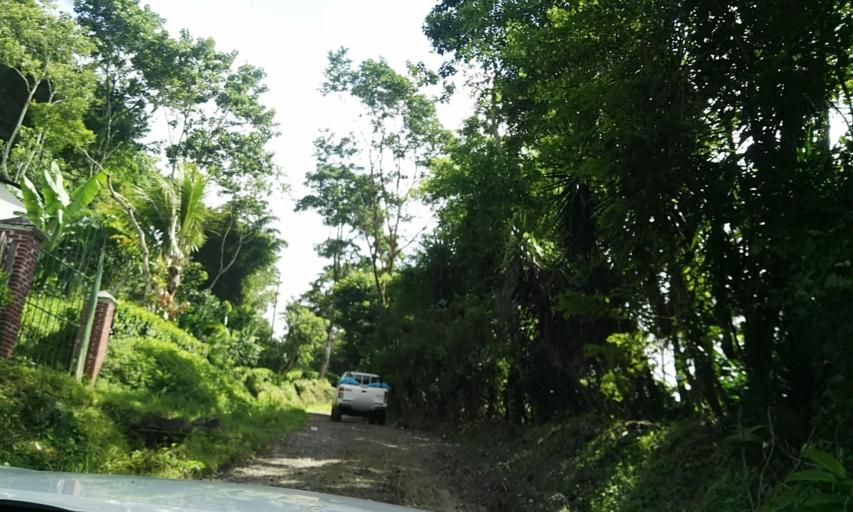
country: NI
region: Matagalpa
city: San Ramon
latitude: 13.0022
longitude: -85.8716
